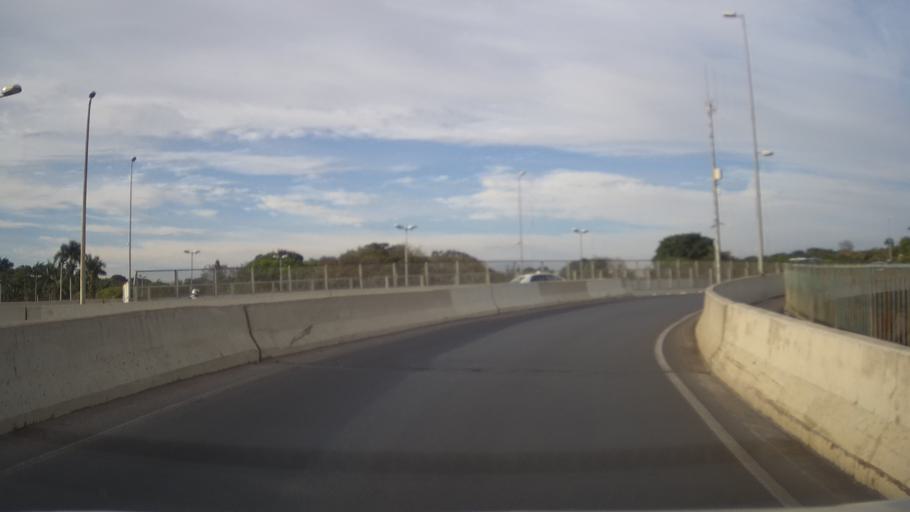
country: BR
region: Minas Gerais
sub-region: Belo Horizonte
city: Belo Horizonte
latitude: -19.8599
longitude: -43.9582
